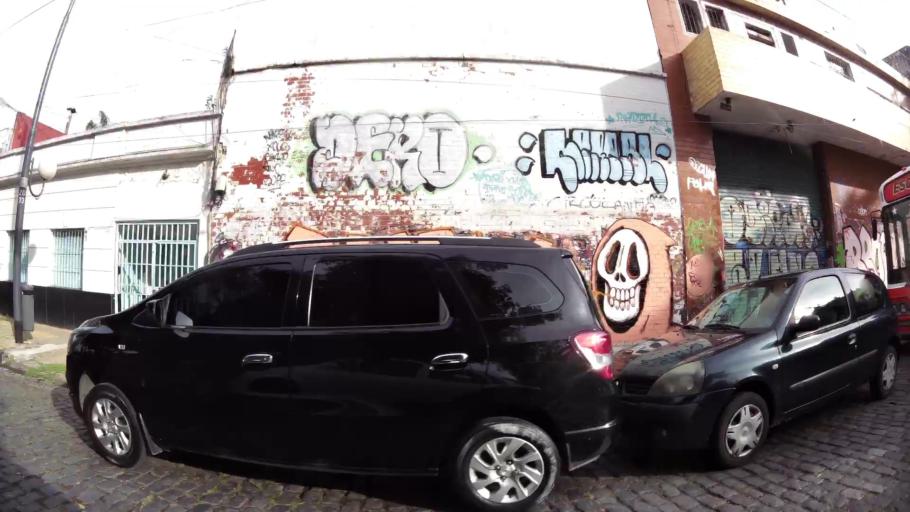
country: AR
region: Buenos Aires F.D.
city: Villa Santa Rita
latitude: -34.6411
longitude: -58.4687
